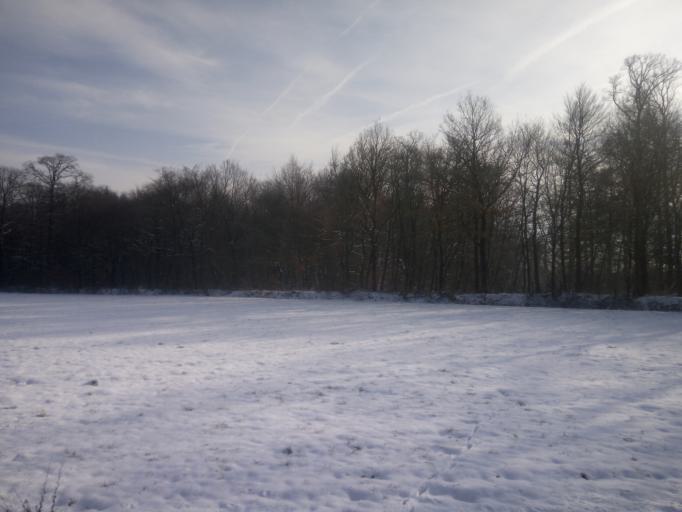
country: LU
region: Grevenmacher
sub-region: Canton d'Echternach
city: Consdorf
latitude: 49.7650
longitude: 6.3376
